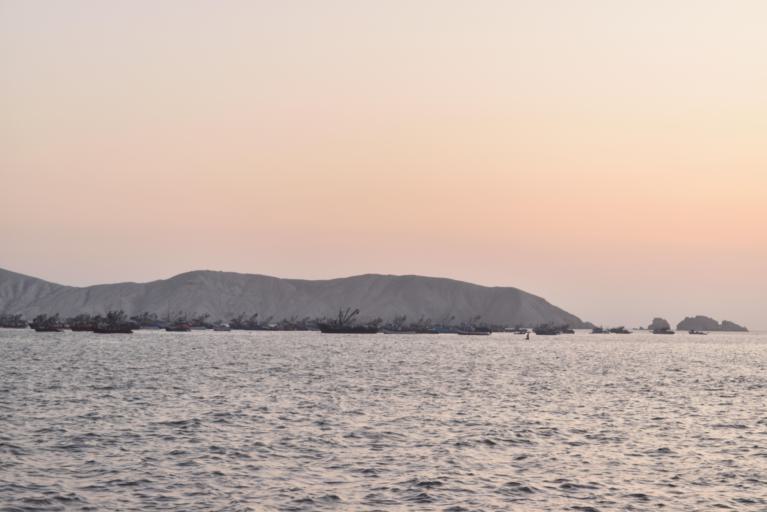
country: PE
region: Ancash
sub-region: Provincia de Santa
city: Chimbote
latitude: -9.0792
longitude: -78.5890
